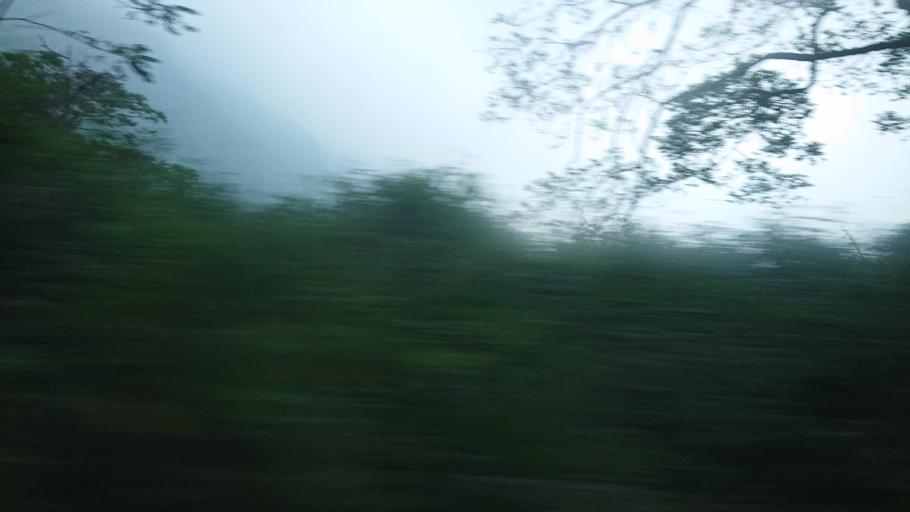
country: TW
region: Taiwan
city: Lugu
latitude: 23.5960
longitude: 120.7182
